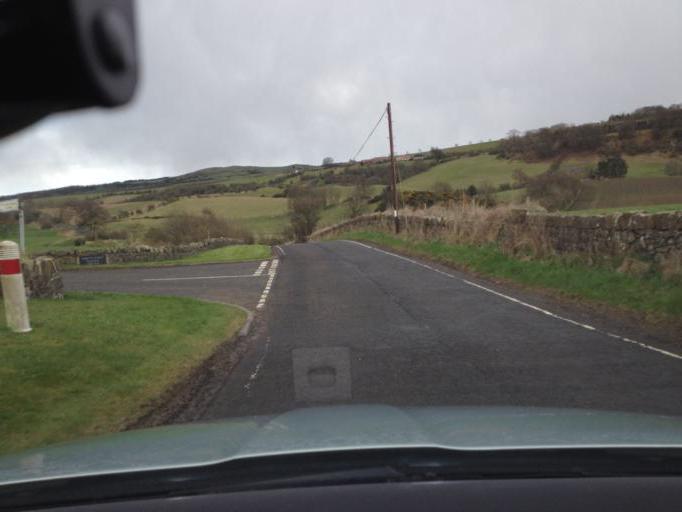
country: GB
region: Scotland
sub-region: West Lothian
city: Linlithgow
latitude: 55.9661
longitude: -3.5956
